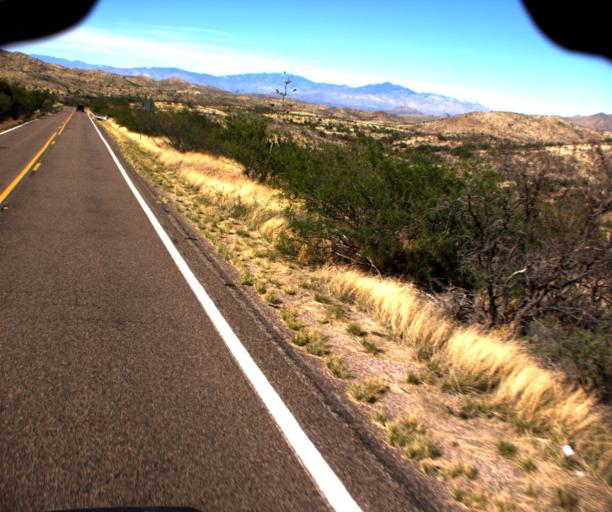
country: US
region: Arizona
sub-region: Pima County
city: Corona de Tucson
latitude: 31.8449
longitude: -110.6992
